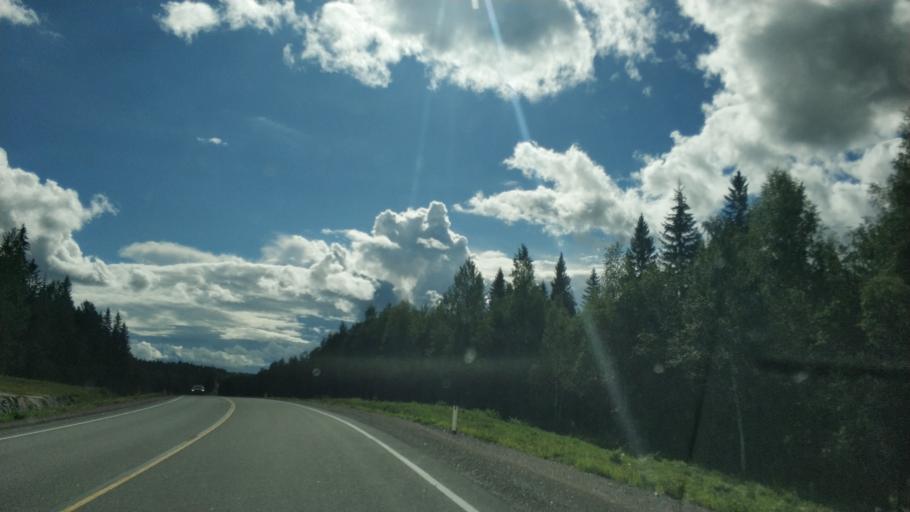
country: RU
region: Republic of Karelia
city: Ruskeala
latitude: 61.8621
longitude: 30.6524
